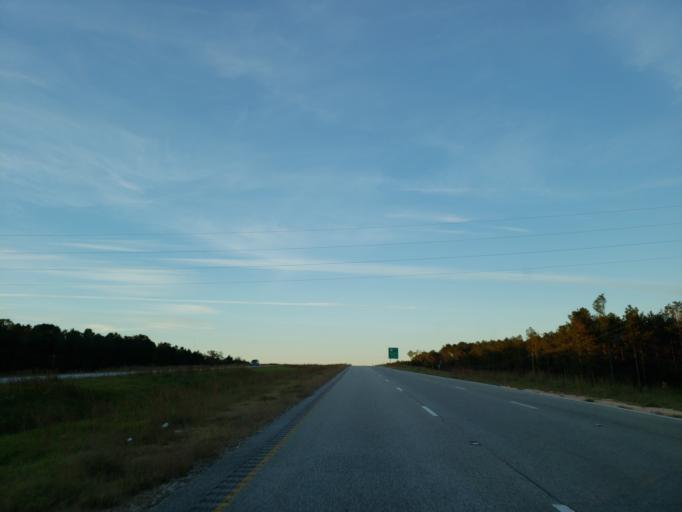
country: US
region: Mississippi
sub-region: Wayne County
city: Belmont
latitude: 31.4422
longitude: -88.4653
